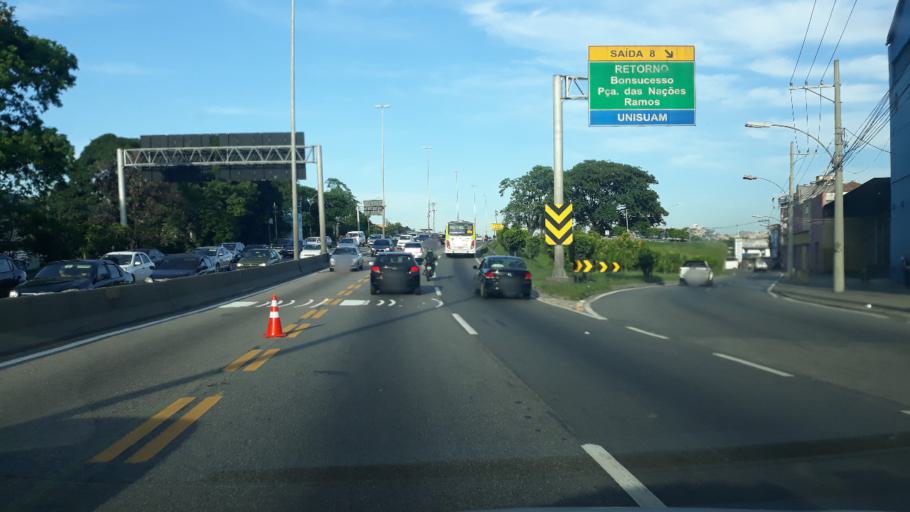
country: BR
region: Rio de Janeiro
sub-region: Rio De Janeiro
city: Rio de Janeiro
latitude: -22.8721
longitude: -43.2511
